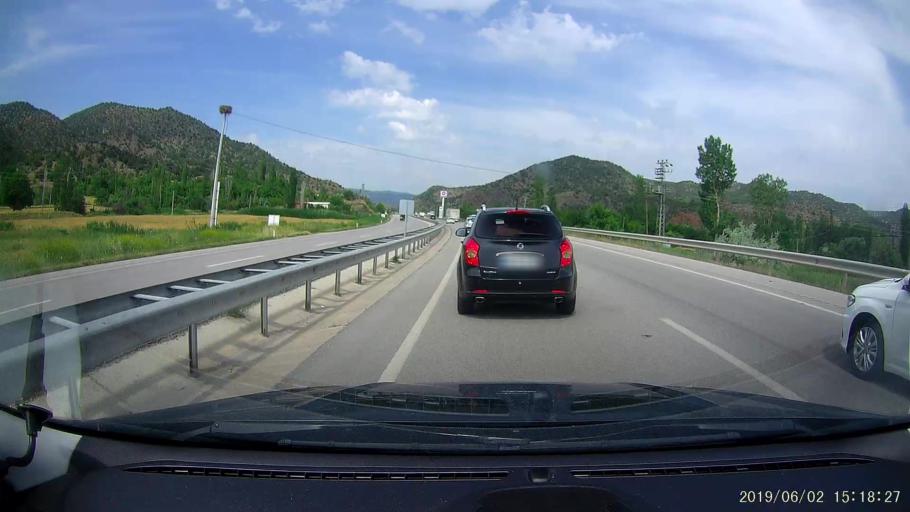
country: TR
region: Corum
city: Osmancik
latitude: 40.9618
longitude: 34.8965
